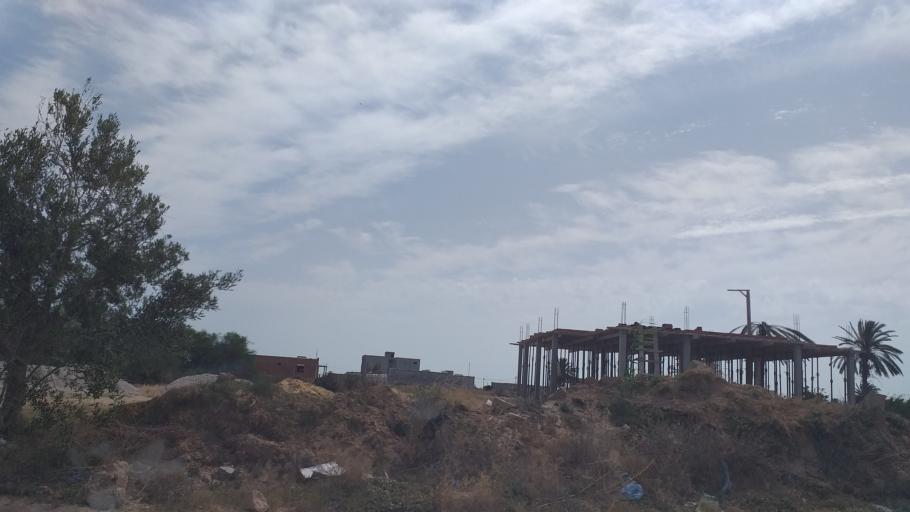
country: TN
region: Qabis
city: Gabes
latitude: 33.9532
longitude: 10.0633
